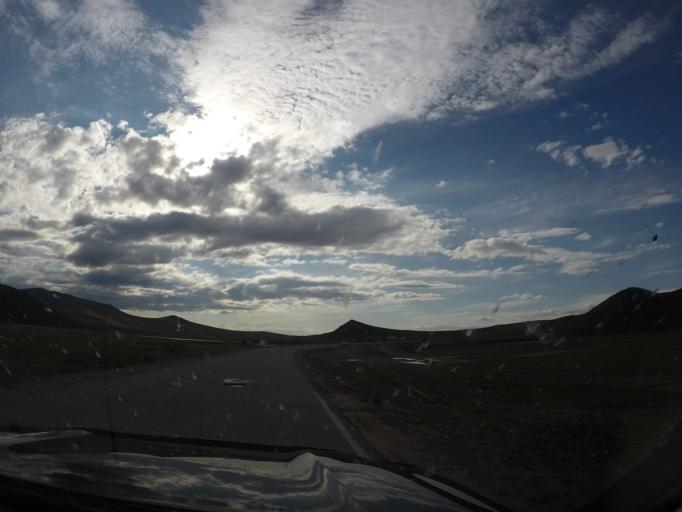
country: MN
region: Central Aimak
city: Bayandelger
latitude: 47.6927
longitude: 108.4745
